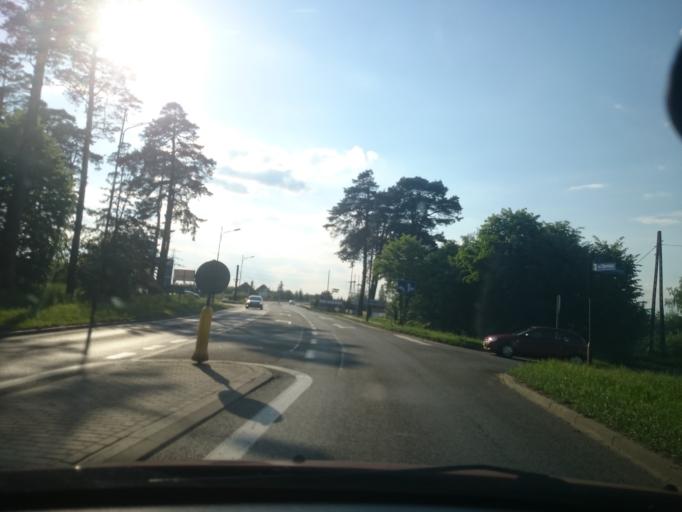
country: PL
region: Opole Voivodeship
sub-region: Powiat strzelecki
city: Strzelce Opolskie
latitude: 50.5201
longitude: 18.2833
